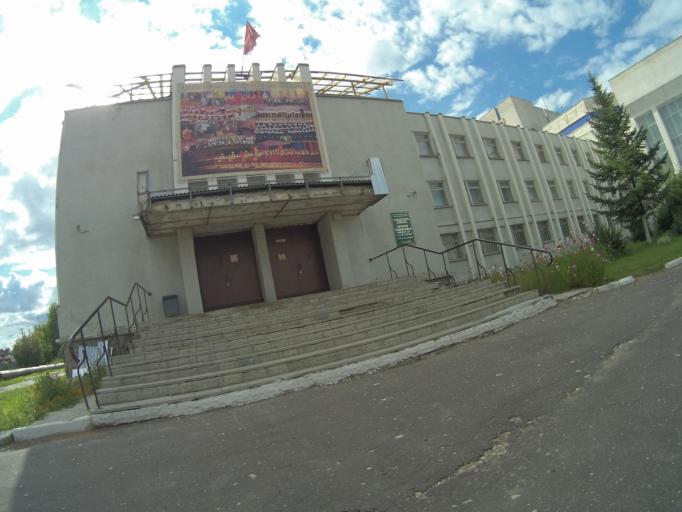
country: RU
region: Vladimir
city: Vladimir
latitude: 56.1172
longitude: 40.3719
